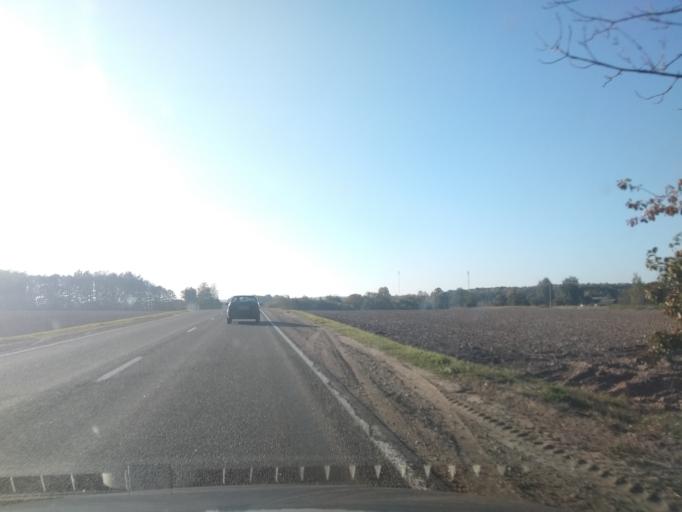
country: BY
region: Grodnenskaya
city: Vyalikaya Byerastavitsa
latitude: 53.1174
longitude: 23.9332
